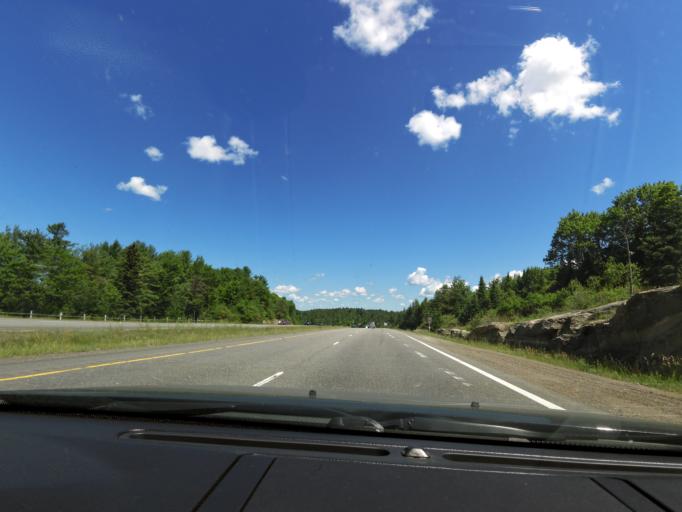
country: CA
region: Ontario
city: Bracebridge
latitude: 45.0799
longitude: -79.2965
